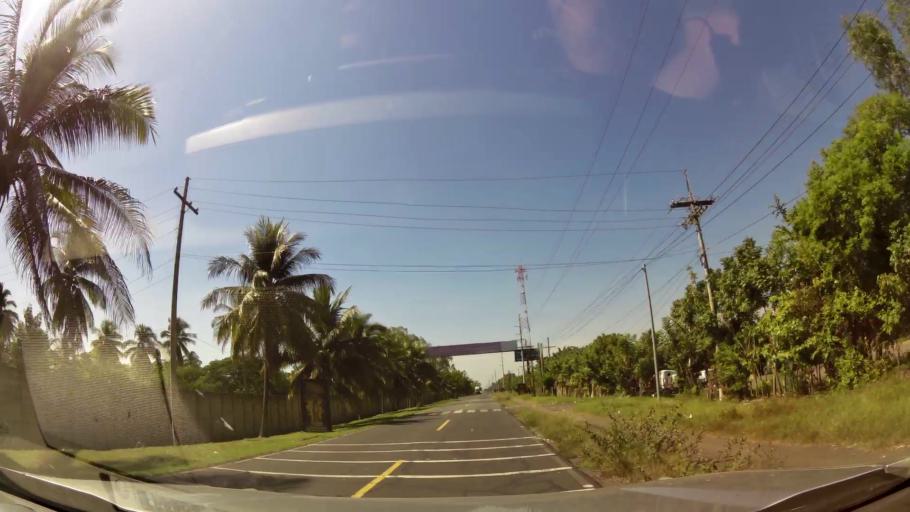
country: GT
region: Escuintla
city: Puerto San Jose
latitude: 13.9333
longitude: -90.7655
